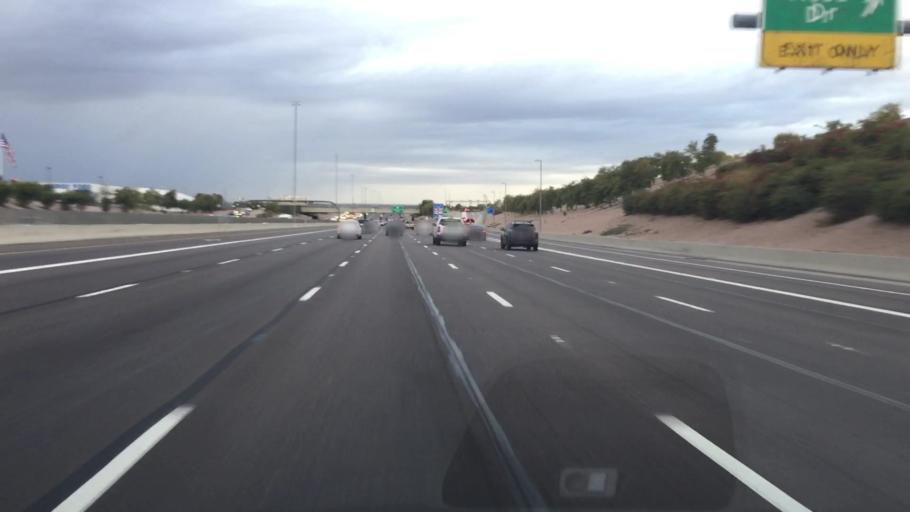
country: US
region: Arizona
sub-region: Maricopa County
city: Mesa
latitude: 33.3854
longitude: -111.8169
